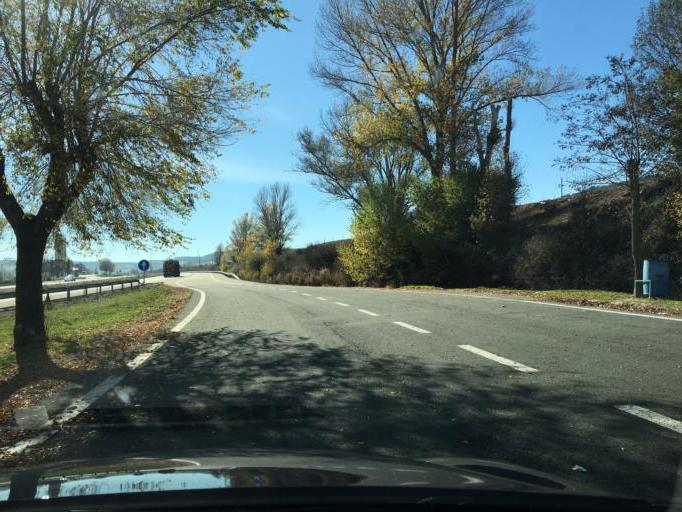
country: ES
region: Castille and Leon
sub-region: Provincia de Burgos
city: Santa Olalla de Bureba
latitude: 42.4697
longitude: -3.4468
